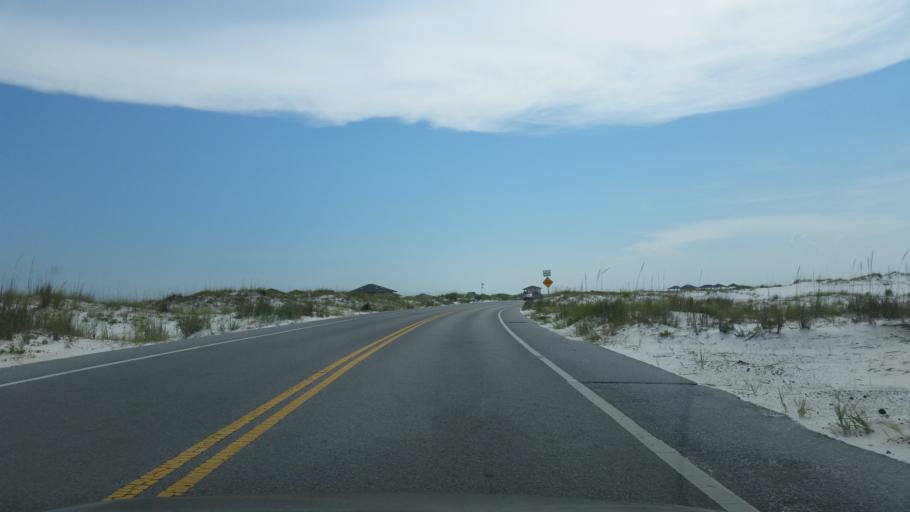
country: US
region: Florida
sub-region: Santa Rosa County
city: Woodlawn Beach
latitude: 30.3650
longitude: -86.9624
